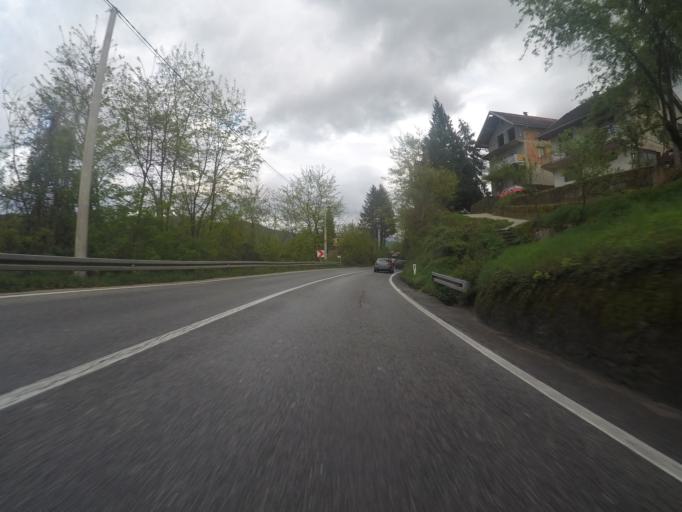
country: BA
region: Federation of Bosnia and Herzegovina
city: Konjic
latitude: 43.6871
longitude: 17.8741
